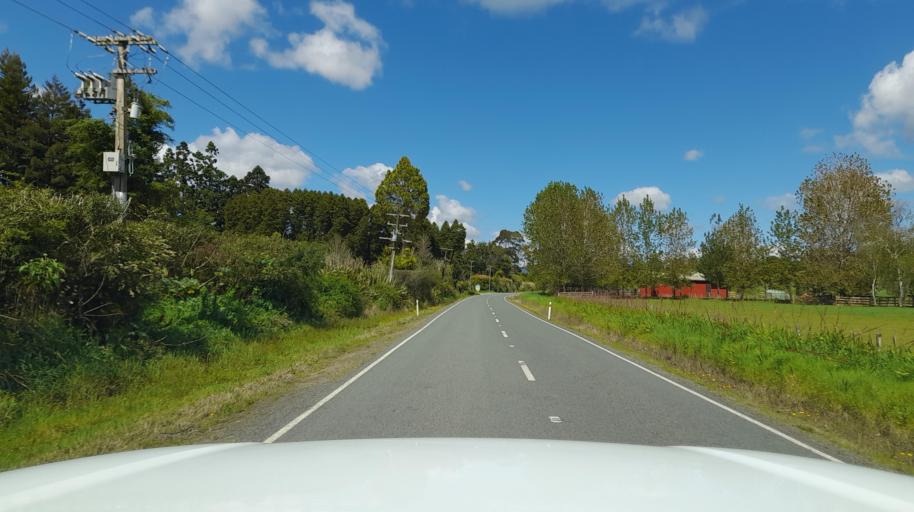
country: NZ
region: Northland
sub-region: Far North District
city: Taipa
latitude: -35.0857
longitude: 173.5093
